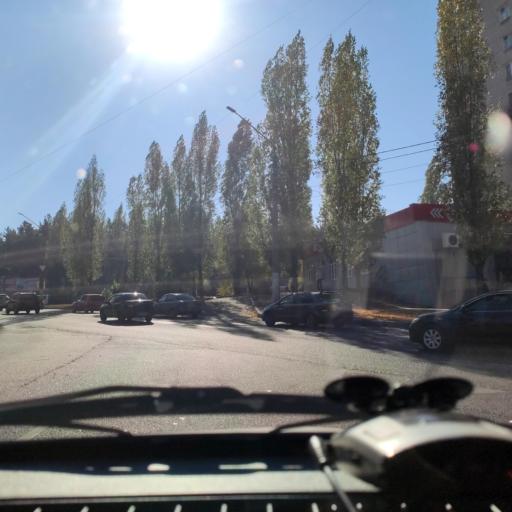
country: RU
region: Voronezj
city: Voronezh
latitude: 51.6557
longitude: 39.1342
